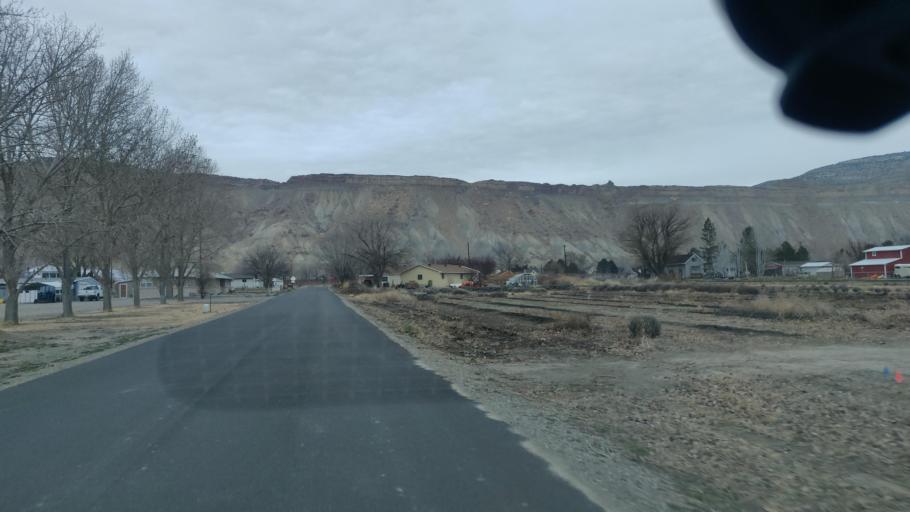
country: US
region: Colorado
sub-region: Mesa County
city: Palisade
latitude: 39.1045
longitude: -108.3853
